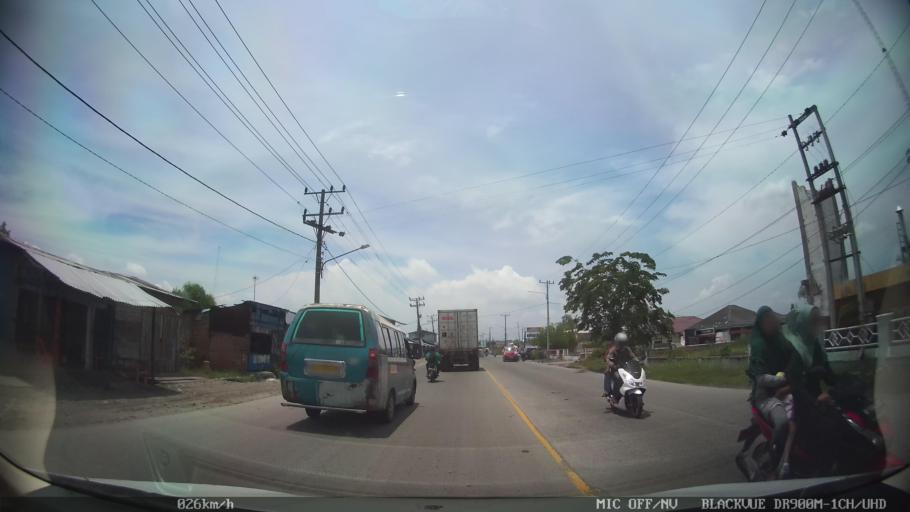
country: ID
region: North Sumatra
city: Belawan
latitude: 3.7648
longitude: 98.6826
